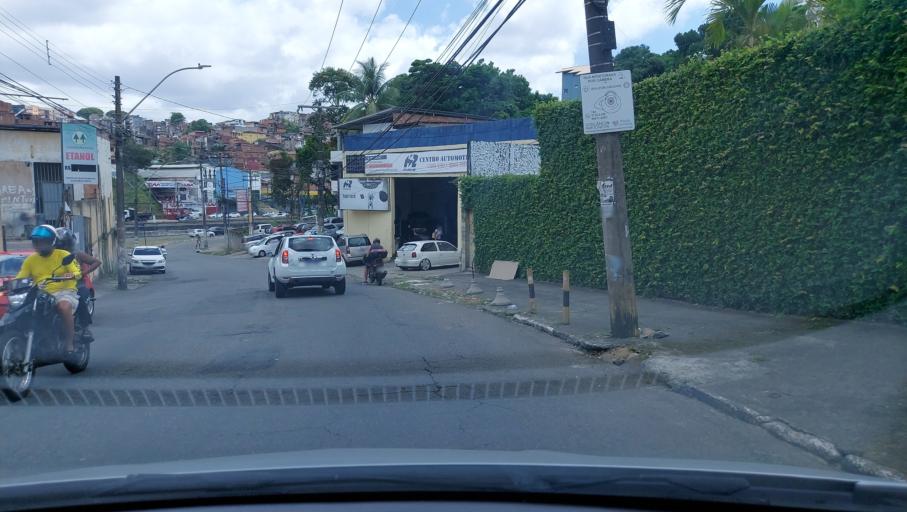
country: BR
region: Bahia
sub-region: Salvador
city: Salvador
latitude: -12.9692
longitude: -38.4879
